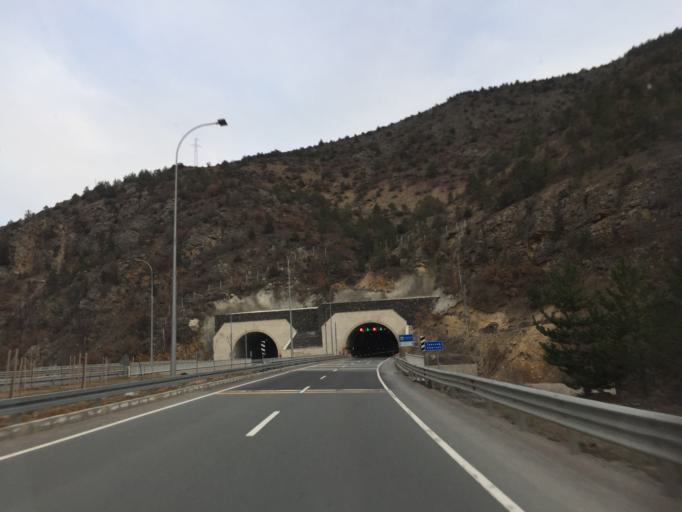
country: TR
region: Gumushane
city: Gumushkhane
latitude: 40.5184
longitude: 39.4106
